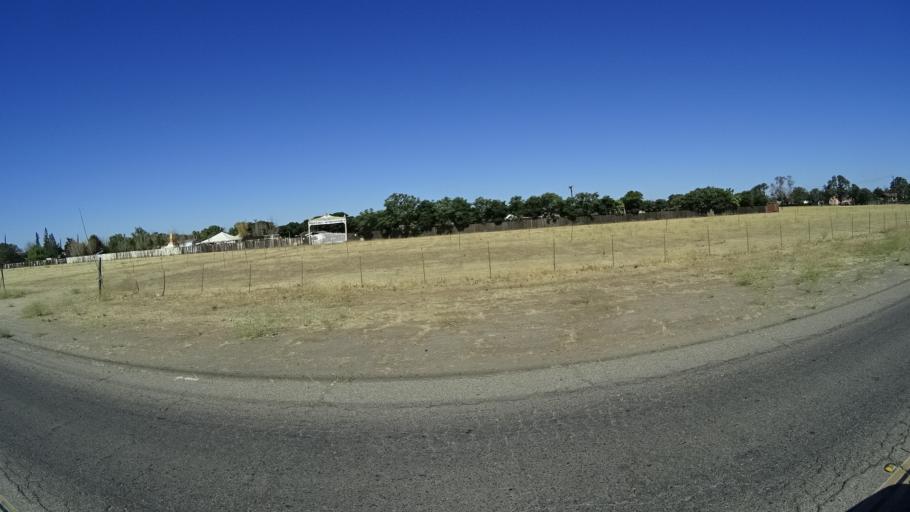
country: US
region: California
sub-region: Fresno County
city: West Park
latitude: 36.7125
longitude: -119.8088
